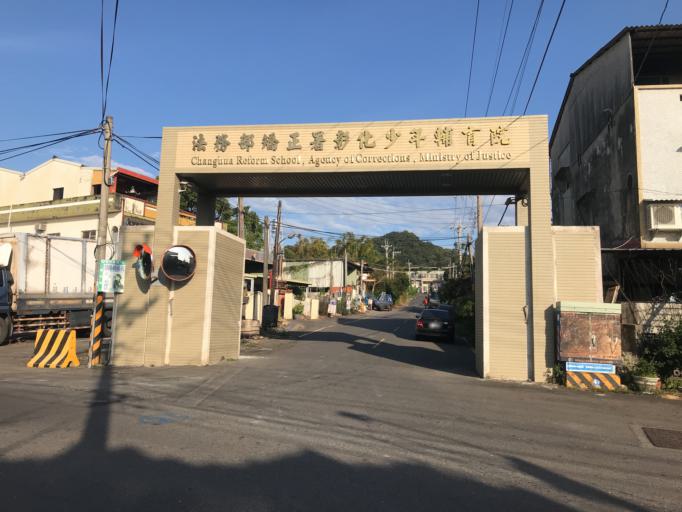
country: TW
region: Taiwan
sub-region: Nantou
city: Nantou
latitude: 23.8765
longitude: 120.6051
